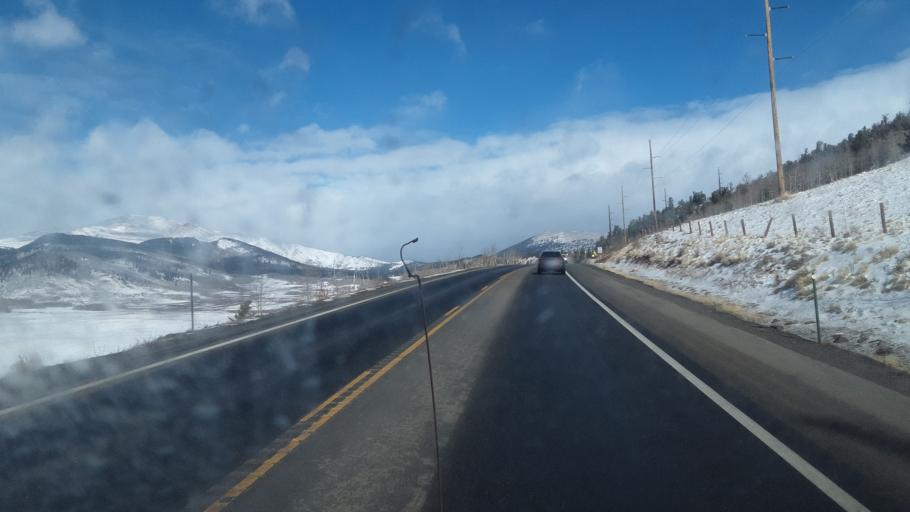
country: US
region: Colorado
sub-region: Park County
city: Fairplay
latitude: 39.2561
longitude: -105.9631
